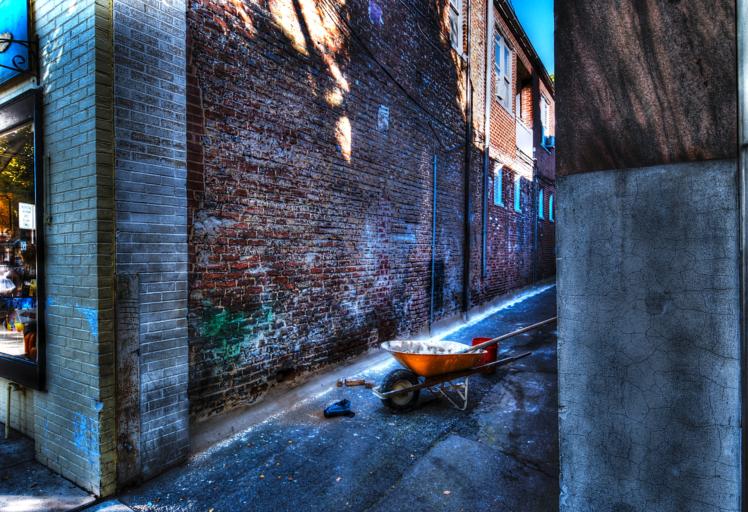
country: US
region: Maryland
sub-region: Frederick County
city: Frederick
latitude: 39.4145
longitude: -77.4108
